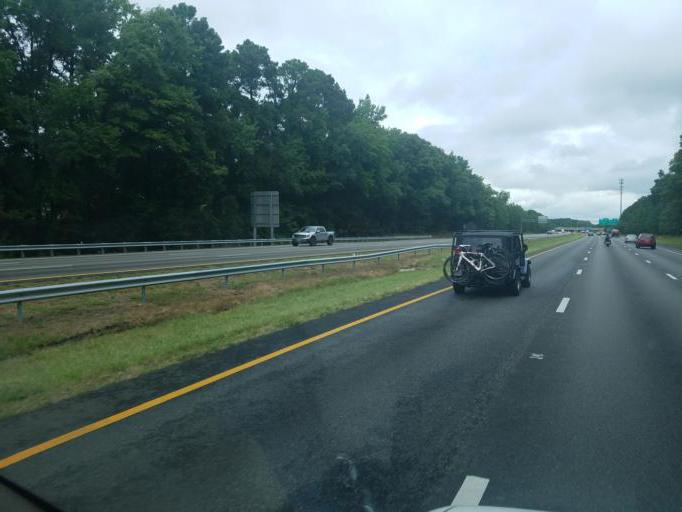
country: US
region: Virginia
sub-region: Henrico County
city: Chamberlayne
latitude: 37.6490
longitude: -77.4516
